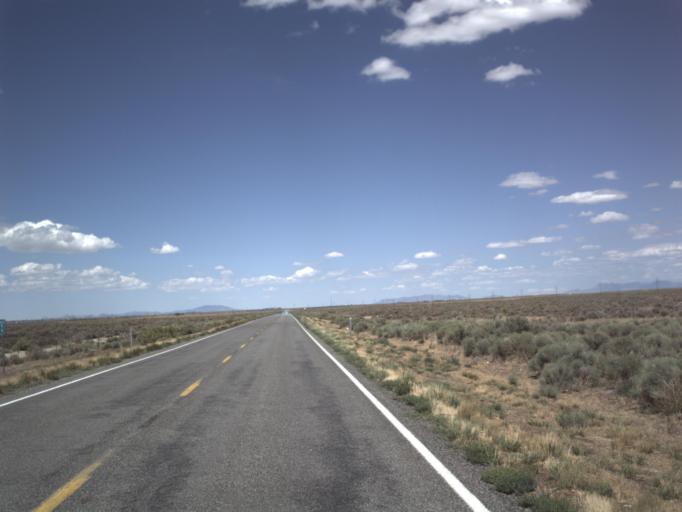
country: US
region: Utah
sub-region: Millard County
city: Delta
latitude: 39.2705
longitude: -112.4540
